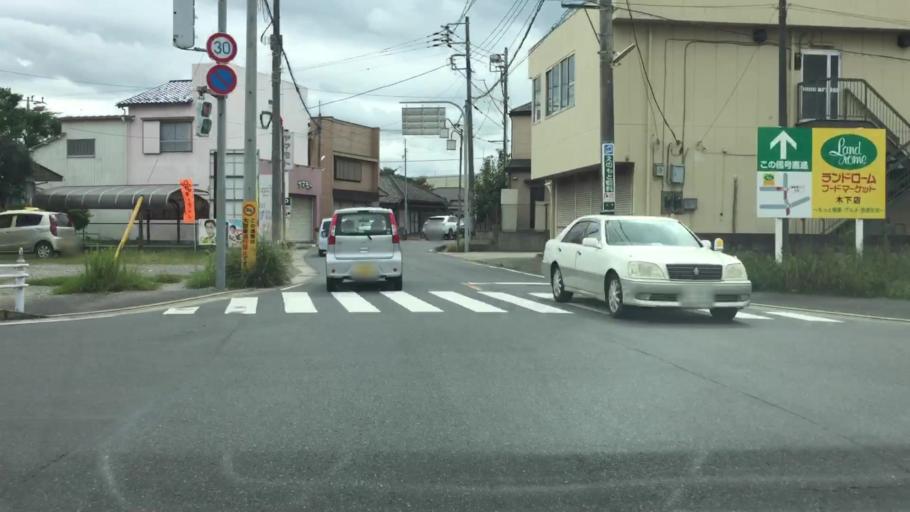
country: JP
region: Ibaraki
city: Ryugasaki
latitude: 35.8394
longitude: 140.1438
